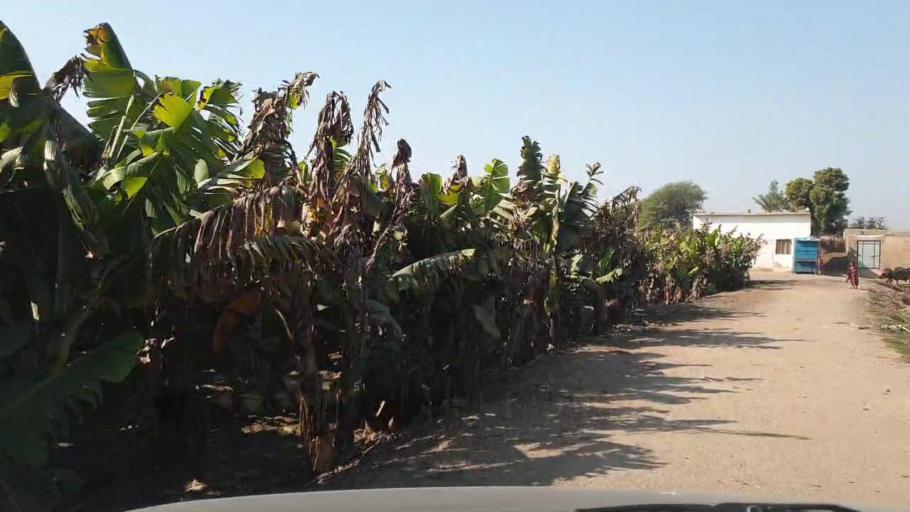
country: PK
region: Sindh
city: Tando Jam
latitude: 25.4412
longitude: 68.5981
